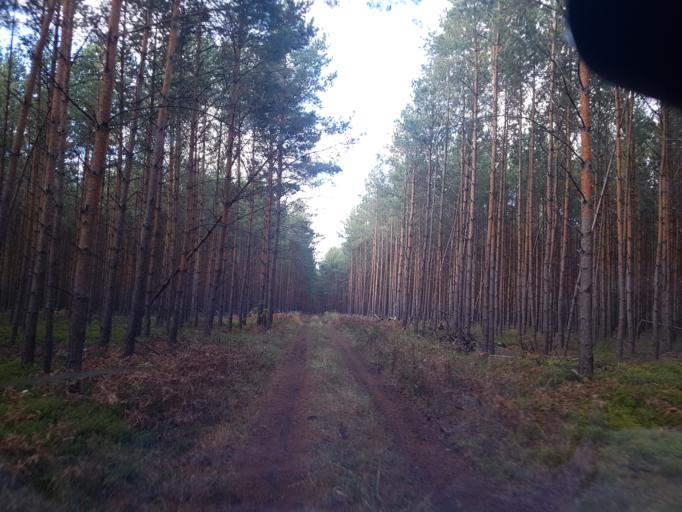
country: DE
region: Brandenburg
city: Finsterwalde
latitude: 51.5572
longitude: 13.6985
